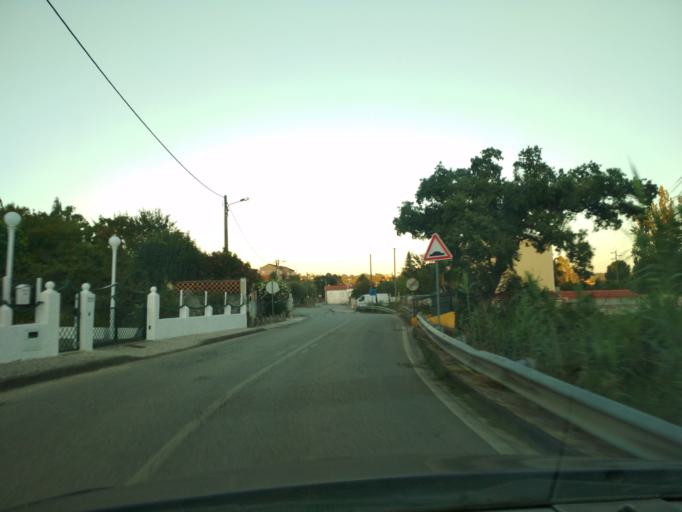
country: PT
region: Coimbra
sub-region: Condeixa-A-Nova
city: Condeixa-a-Nova
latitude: 40.1678
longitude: -8.4719
